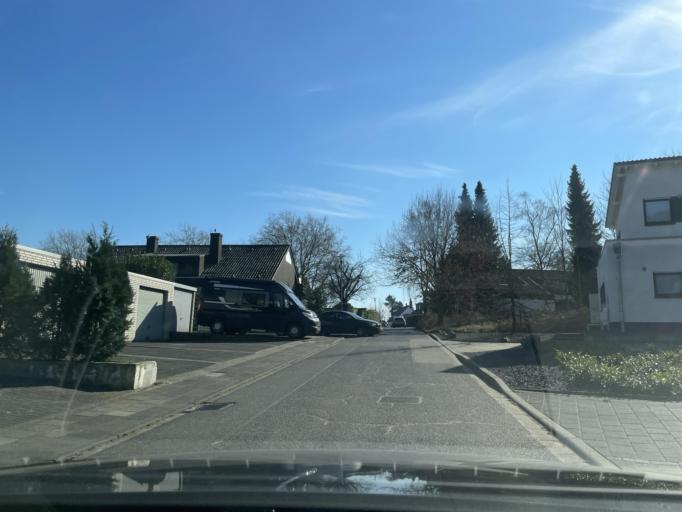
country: DE
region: North Rhine-Westphalia
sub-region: Regierungsbezirk Dusseldorf
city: Monchengladbach
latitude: 51.2135
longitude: 6.4424
